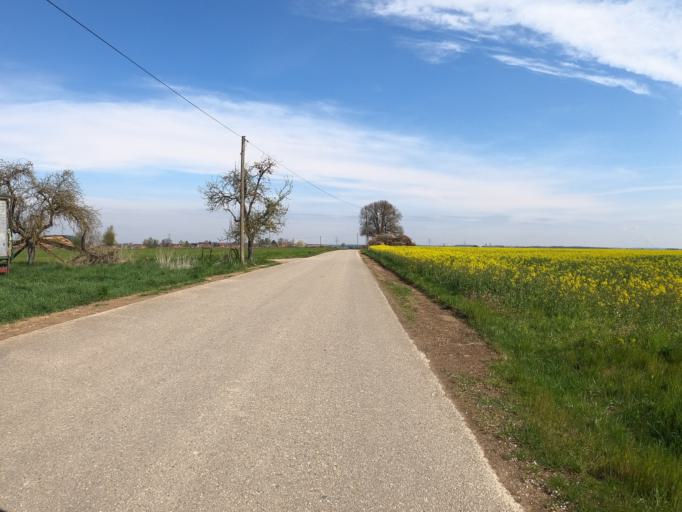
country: DE
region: Bavaria
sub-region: Swabia
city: Rieden an der Kotz
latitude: 48.3771
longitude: 10.2181
